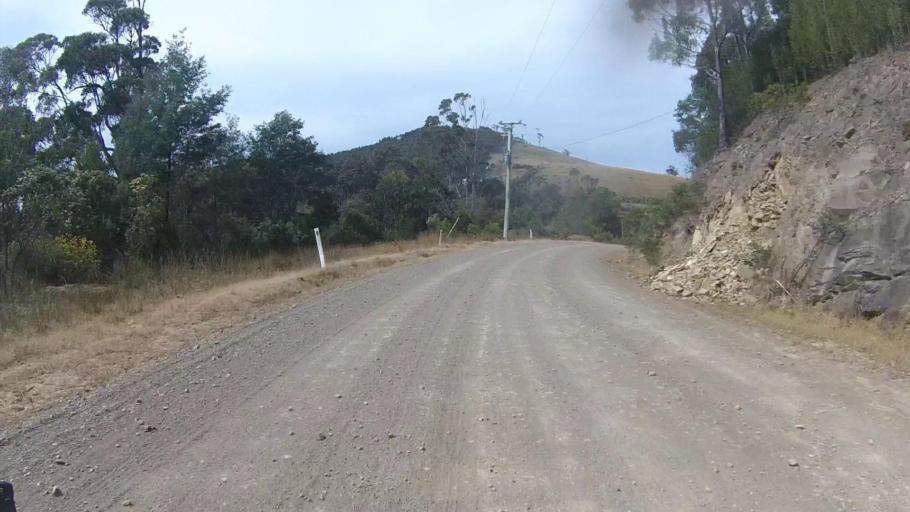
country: AU
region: Tasmania
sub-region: Sorell
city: Sorell
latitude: -42.7734
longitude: 147.8303
